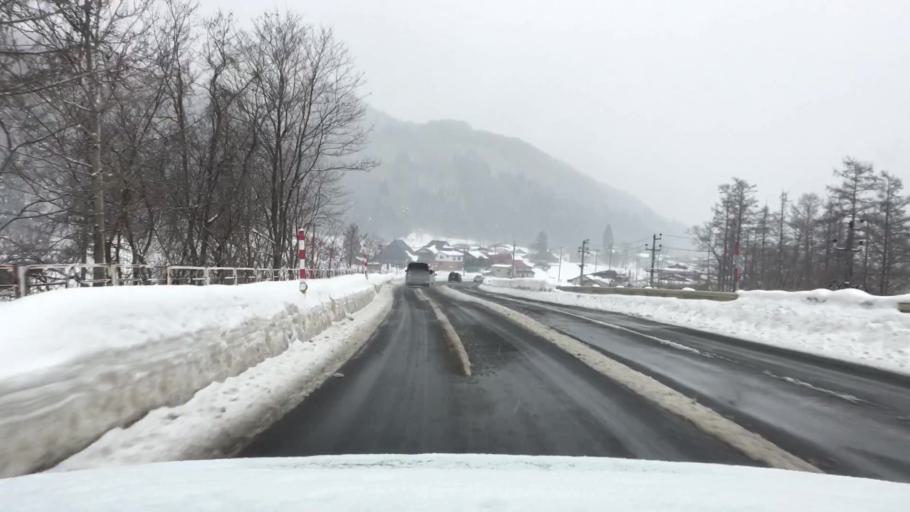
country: JP
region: Akita
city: Hanawa
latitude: 40.0640
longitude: 141.0154
